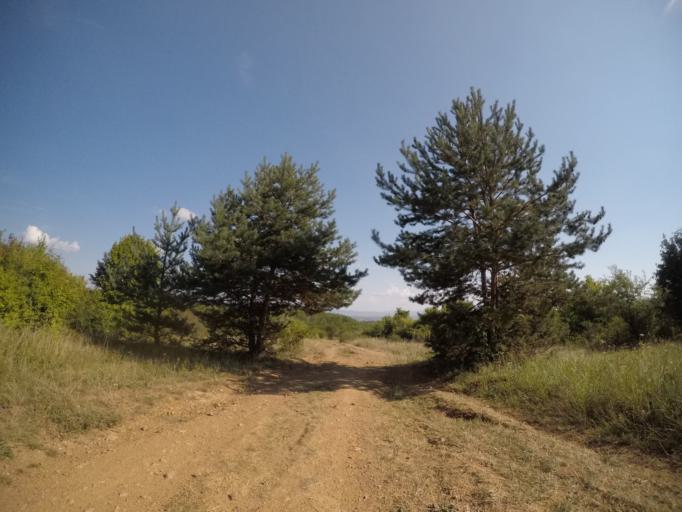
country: SK
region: Kosicky
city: Kosice
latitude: 48.7387
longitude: 21.2098
